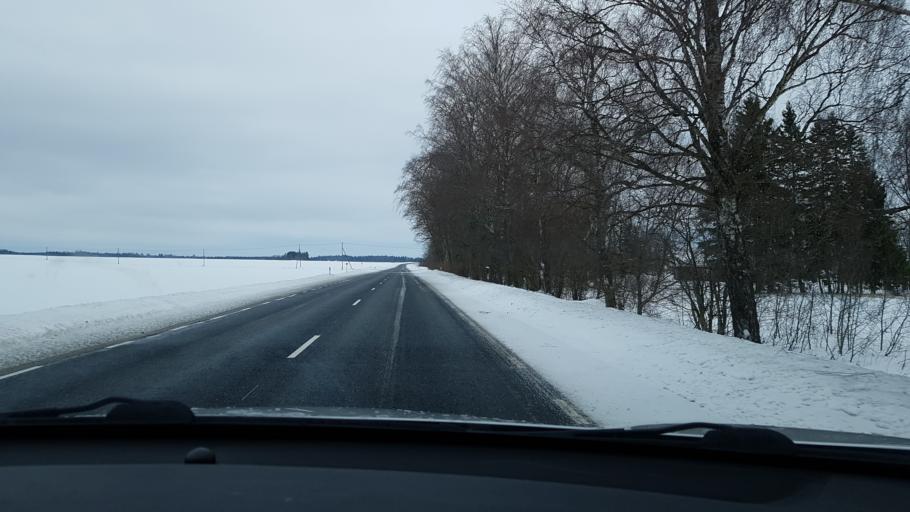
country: EE
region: Jaervamaa
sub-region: Jaerva-Jaani vald
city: Jarva-Jaani
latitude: 59.1224
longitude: 25.7872
